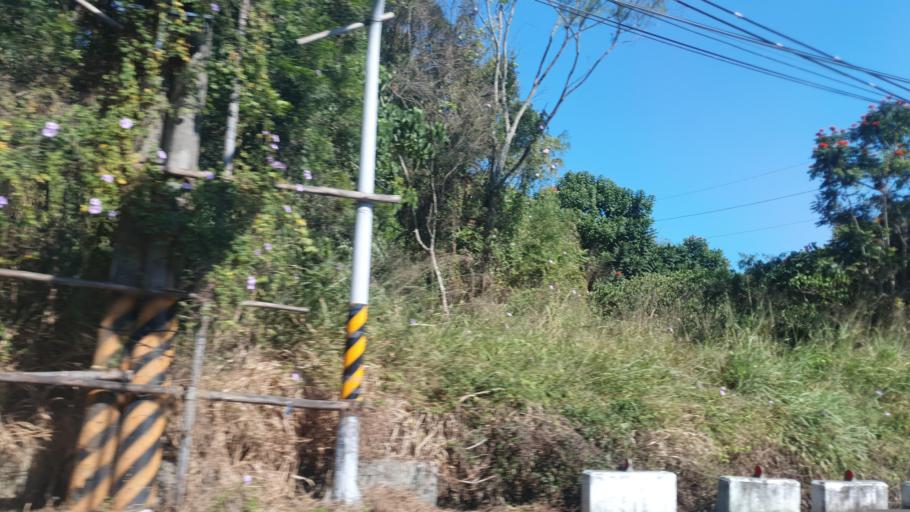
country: TW
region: Taiwan
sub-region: Tainan
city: Tainan
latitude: 23.0343
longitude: 120.3466
